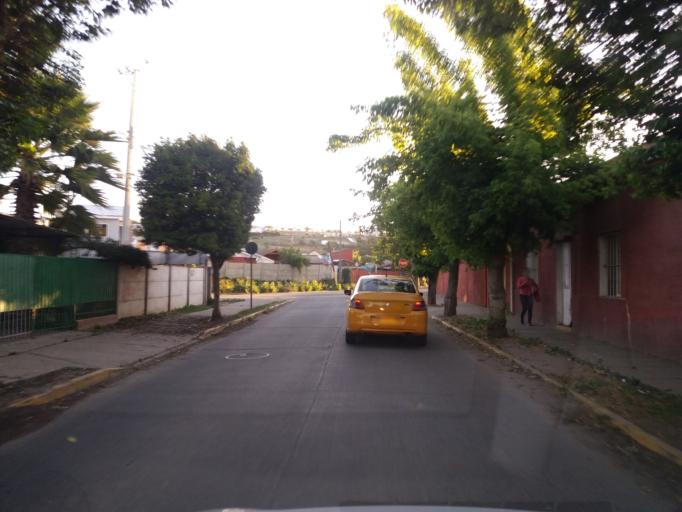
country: CL
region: Valparaiso
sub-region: Provincia de Quillota
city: Quillota
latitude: -32.9381
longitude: -71.2743
